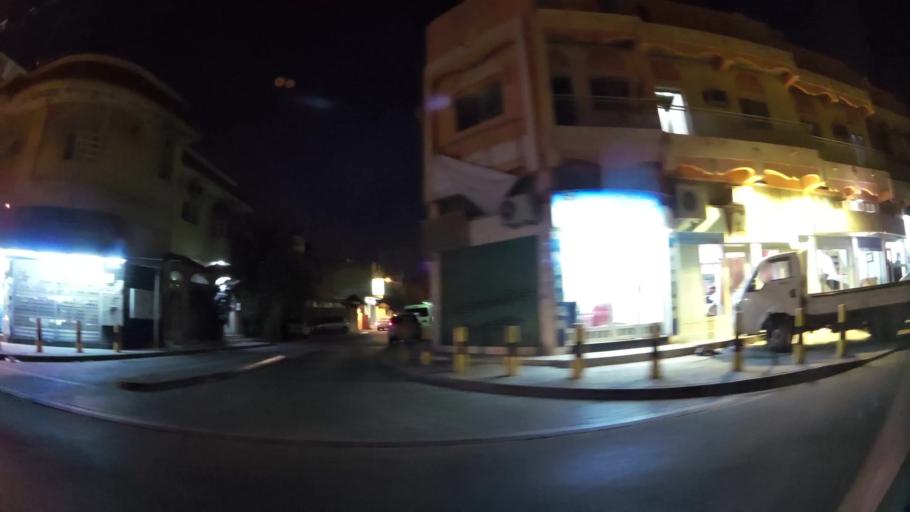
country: BH
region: Manama
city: Jidd Hafs
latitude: 26.2170
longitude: 50.5371
